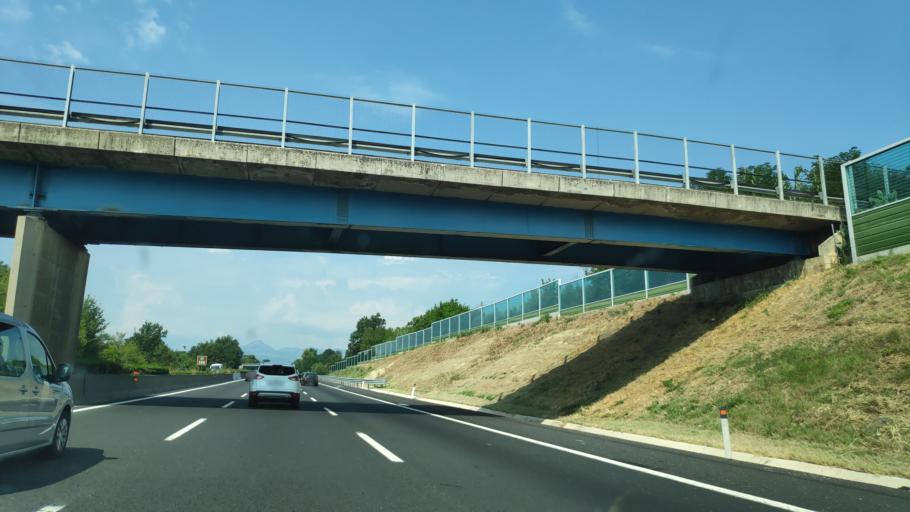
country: IT
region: Latium
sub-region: Provincia di Frosinone
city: Pofi
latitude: 41.5558
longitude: 13.4254
